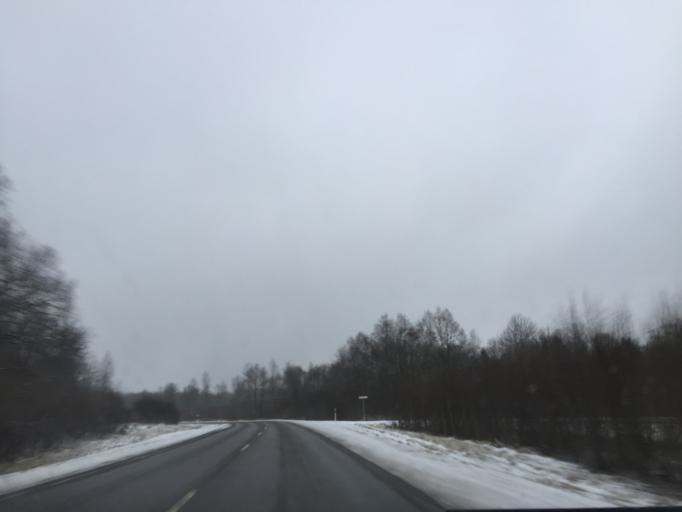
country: EE
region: Laeaene
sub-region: Lihula vald
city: Lihula
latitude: 58.5524
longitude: 23.9872
